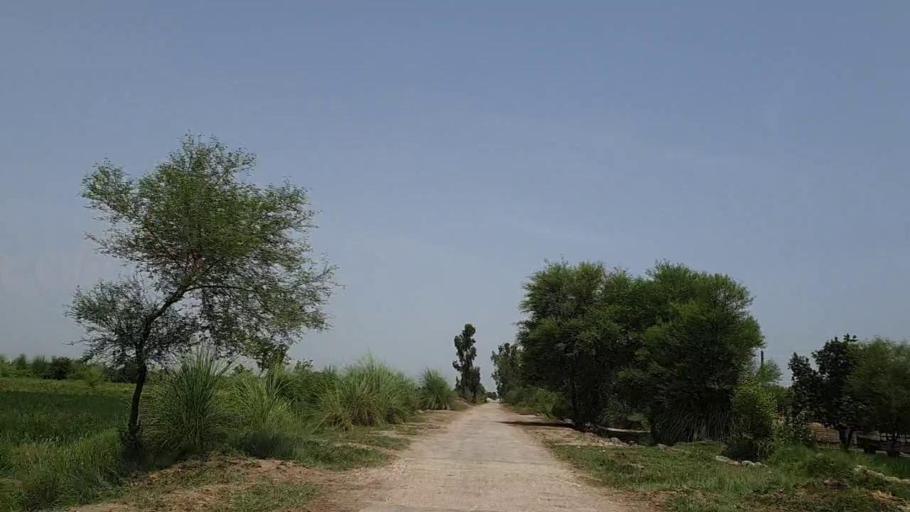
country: PK
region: Sindh
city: Tharu Shah
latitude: 26.9406
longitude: 68.0247
